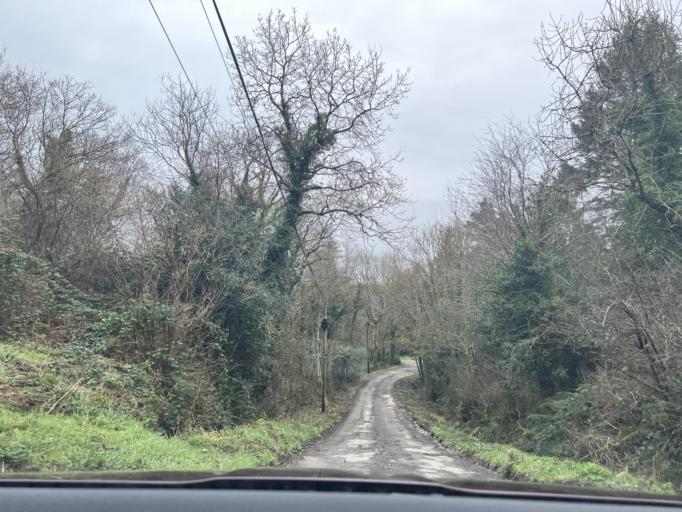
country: IE
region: Leinster
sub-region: Loch Garman
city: Castlebridge
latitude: 52.3862
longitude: -6.5524
